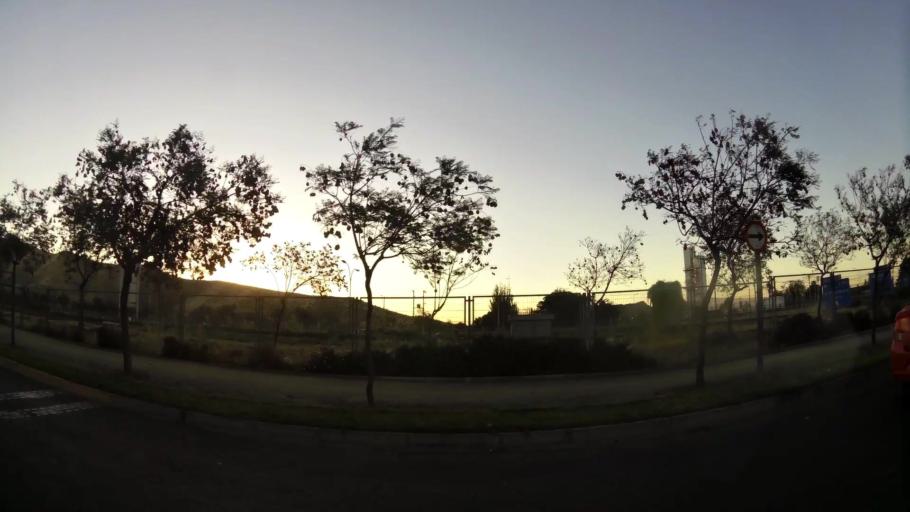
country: CL
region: Santiago Metropolitan
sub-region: Provincia de Maipo
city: San Bernardo
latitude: -33.5746
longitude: -70.7124
